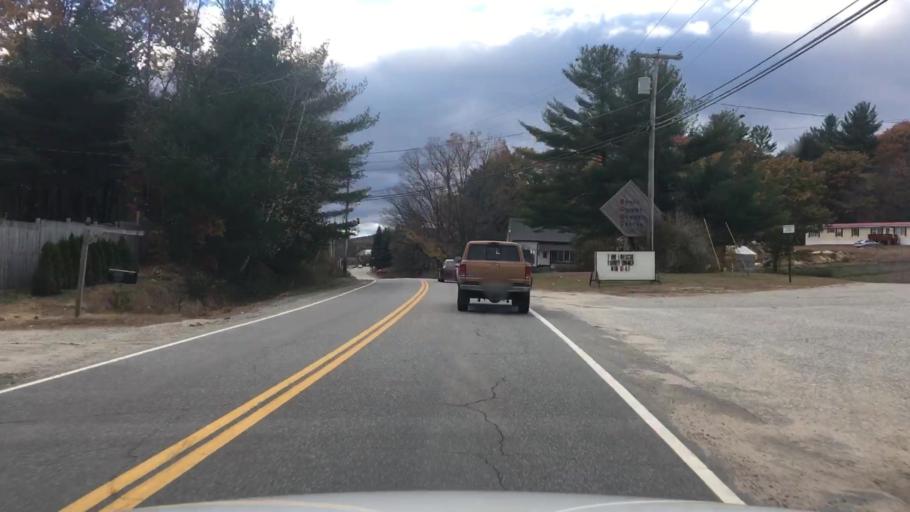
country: US
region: Maine
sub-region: Androscoggin County
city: Livermore
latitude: 44.3406
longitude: -70.2481
